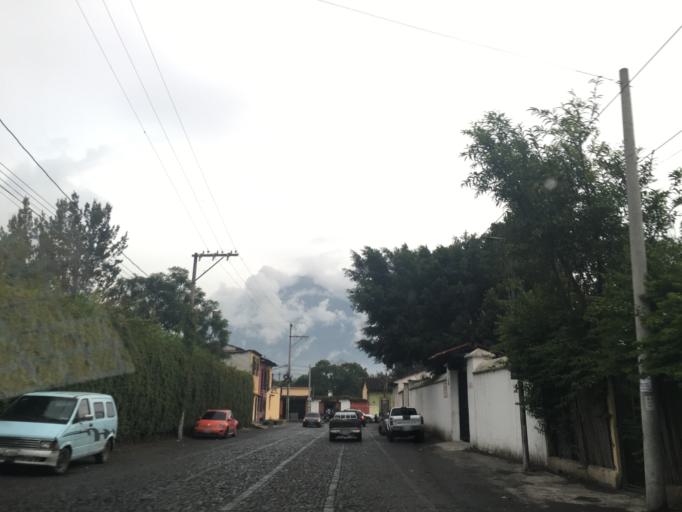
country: GT
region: Sacatepequez
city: Antigua Guatemala
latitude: 14.5570
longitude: -90.7410
